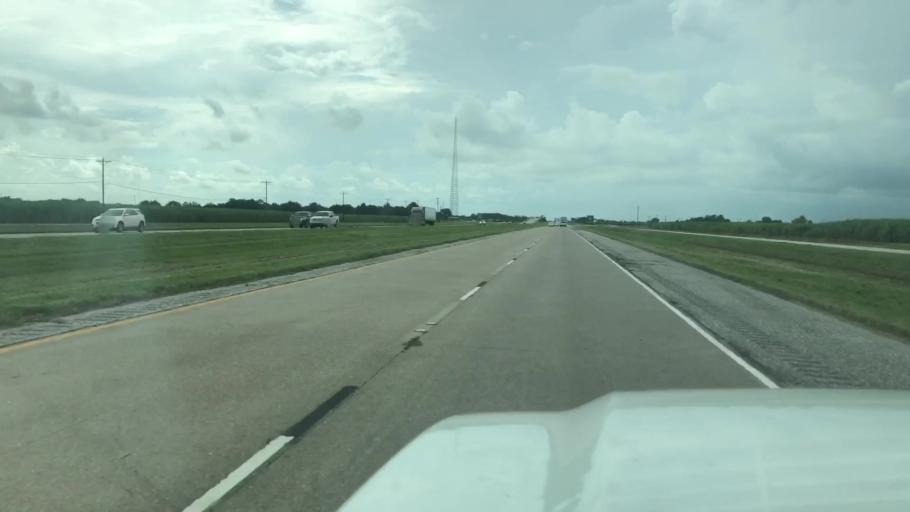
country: US
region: Louisiana
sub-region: Iberia Parish
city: Jeanerette
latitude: 29.9141
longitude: -91.7199
